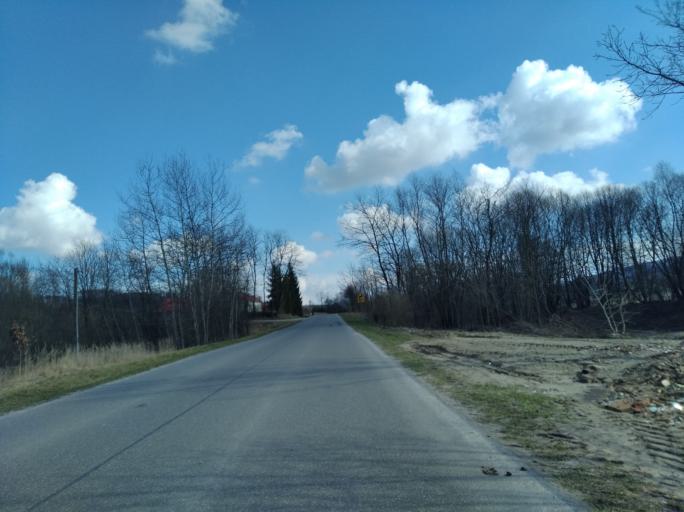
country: PL
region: Subcarpathian Voivodeship
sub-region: Powiat jasielski
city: Kolaczyce
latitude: 49.8590
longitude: 21.4827
